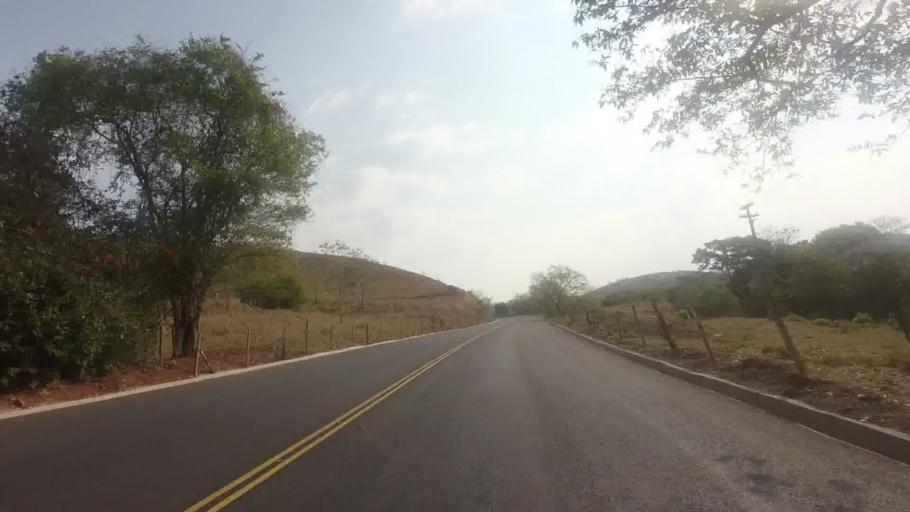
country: BR
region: Rio de Janeiro
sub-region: Itaperuna
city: Itaperuna
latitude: -21.3121
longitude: -41.8586
